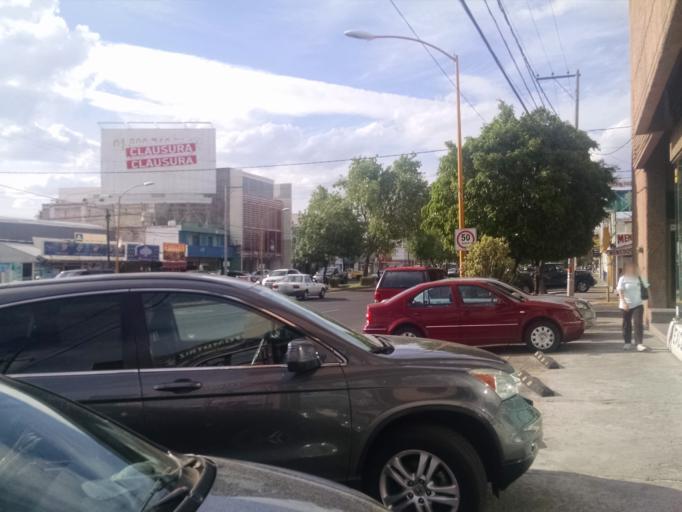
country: MX
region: Aguascalientes
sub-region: Aguascalientes
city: Aguascalientes
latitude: 21.8815
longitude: -102.3123
